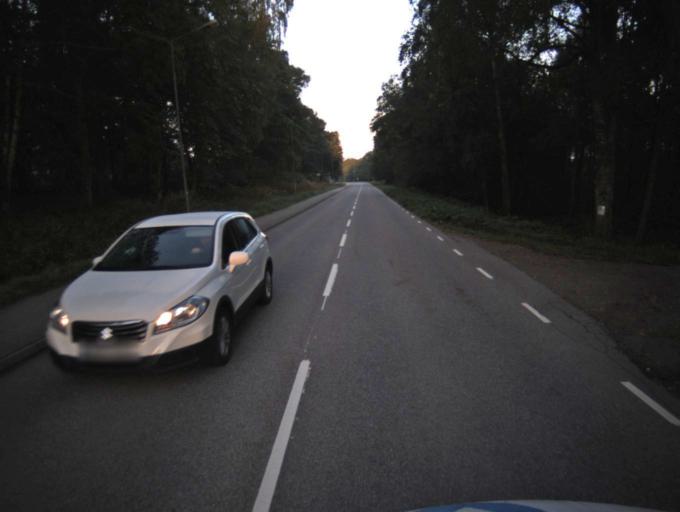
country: SE
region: Vaestra Goetaland
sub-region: Ulricehamns Kommun
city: Ulricehamn
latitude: 57.8037
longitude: 13.4380
